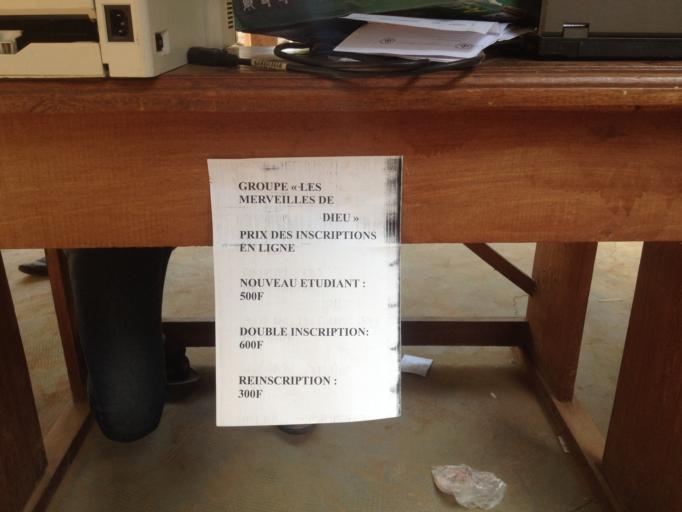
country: BJ
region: Borgou
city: Parakou
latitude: 9.3375
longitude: 2.6452
